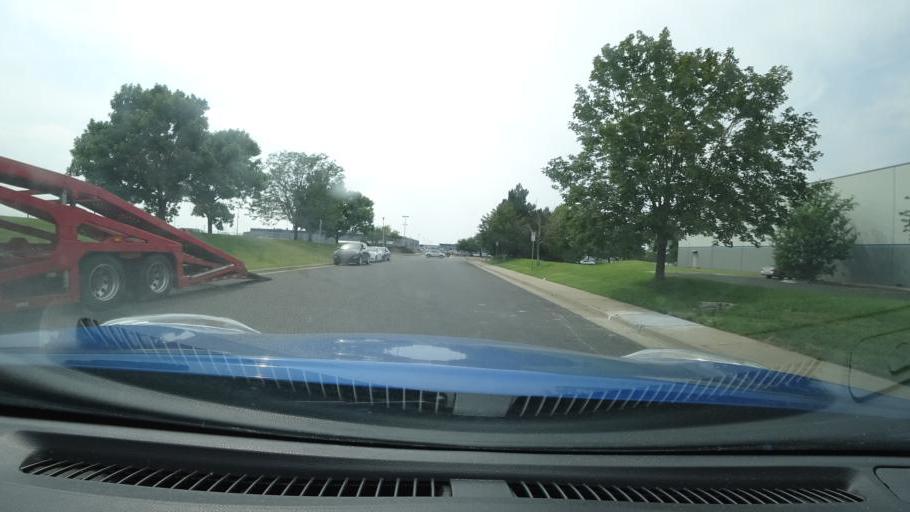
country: US
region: Colorado
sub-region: Adams County
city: Aurora
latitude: 39.7583
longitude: -104.7818
